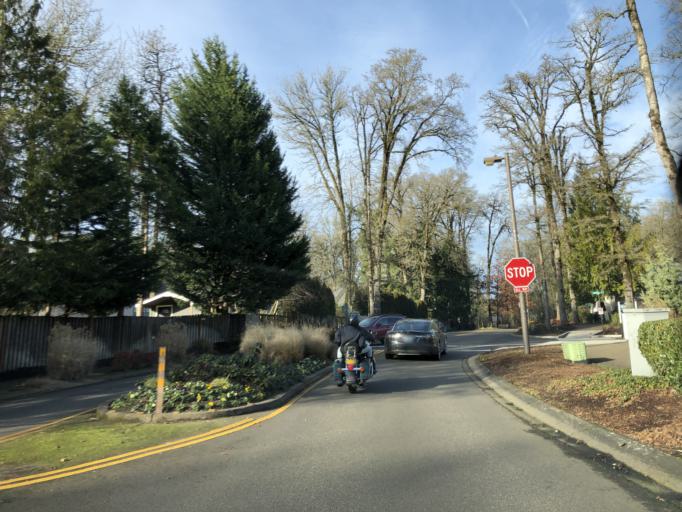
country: US
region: Oregon
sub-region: Washington County
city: Durham
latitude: 45.4205
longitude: -122.7327
